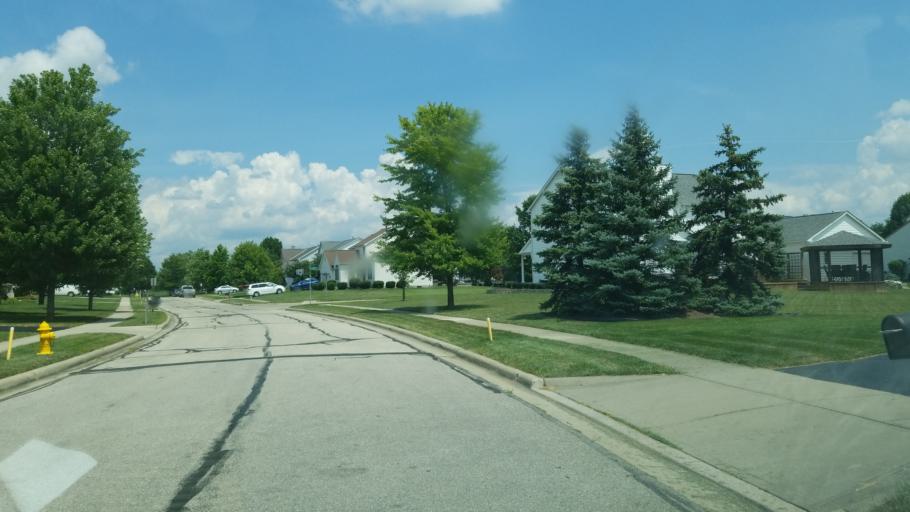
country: US
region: Ohio
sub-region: Delaware County
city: Lewis Center
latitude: 40.2177
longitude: -82.9956
